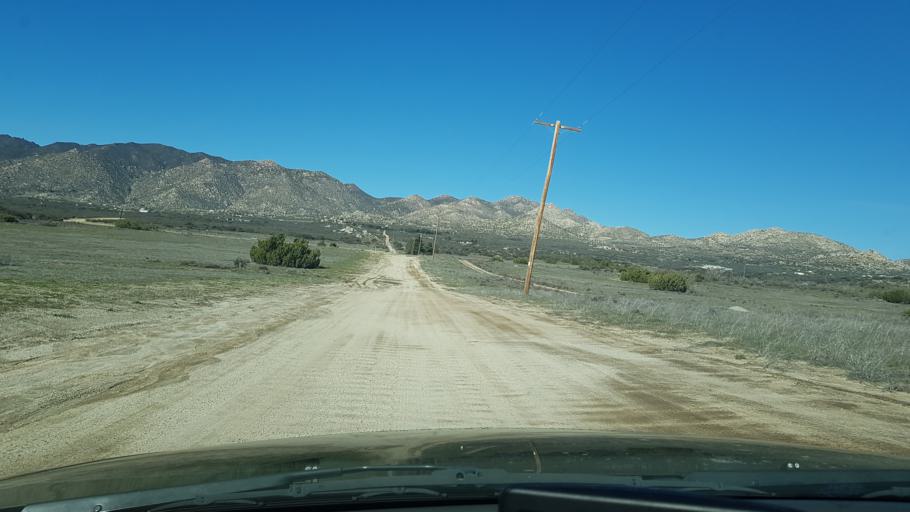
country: US
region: California
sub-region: San Diego County
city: Borrego Springs
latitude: 33.2065
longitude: -116.5081
